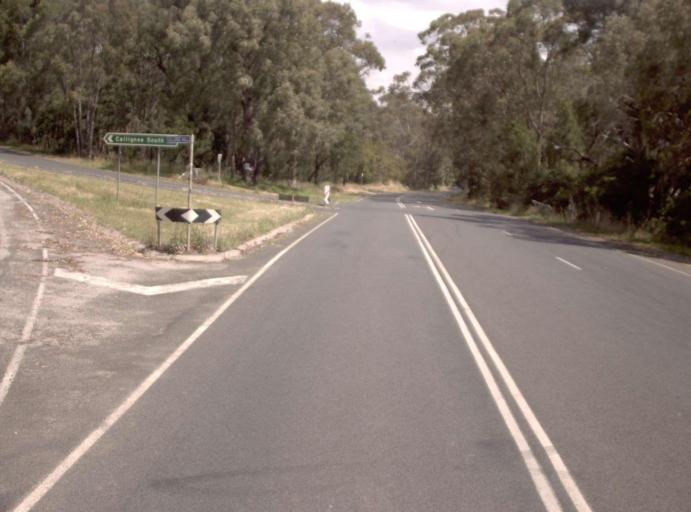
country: AU
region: Victoria
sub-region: Latrobe
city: Traralgon
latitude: -38.2773
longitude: 146.5482
